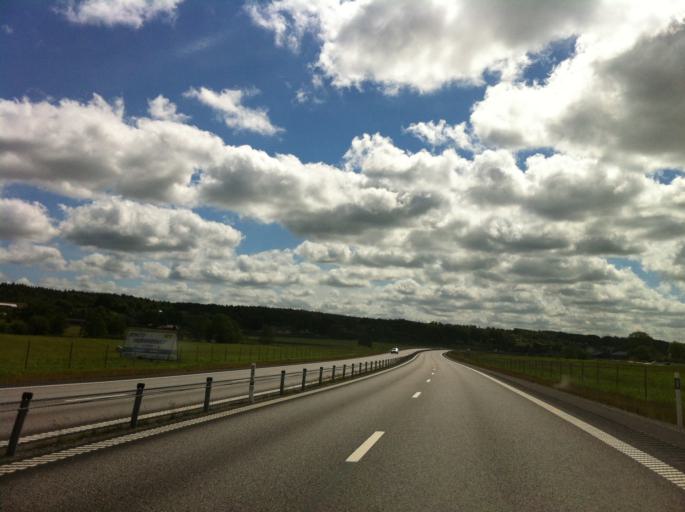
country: SE
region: Vaestra Goetaland
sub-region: Ale Kommun
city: Skepplanda
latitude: 57.9795
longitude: 12.1606
